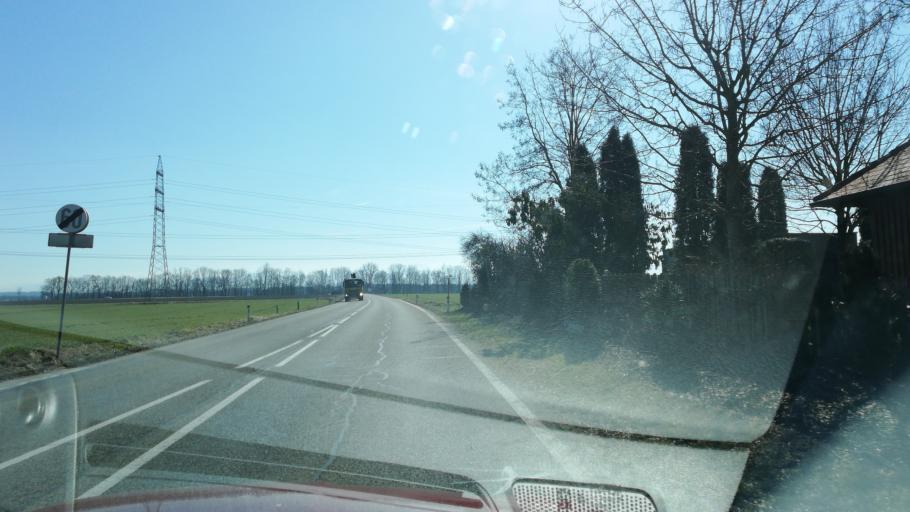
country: AT
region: Upper Austria
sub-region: Wels-Land
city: Neukirchen bei Lambach
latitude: 48.0922
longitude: 13.8390
